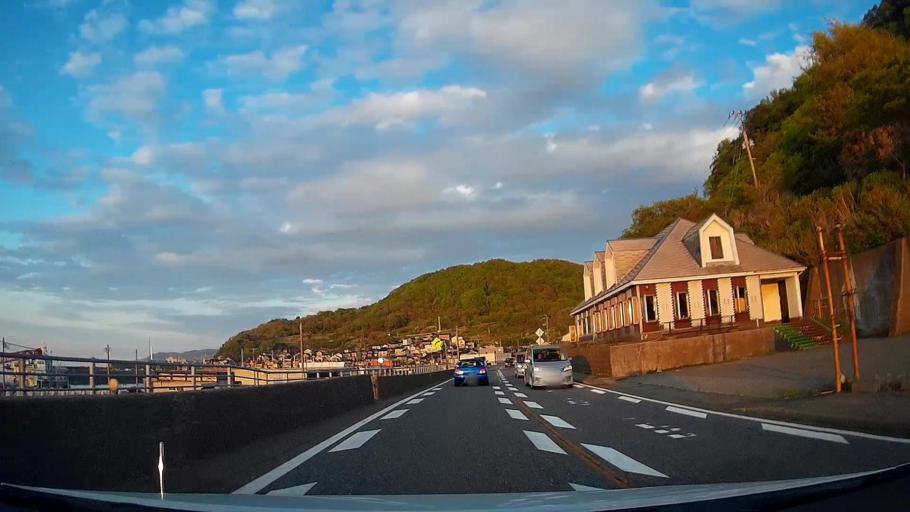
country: JP
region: Niigata
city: Itoigawa
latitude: 37.1090
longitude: 137.9949
